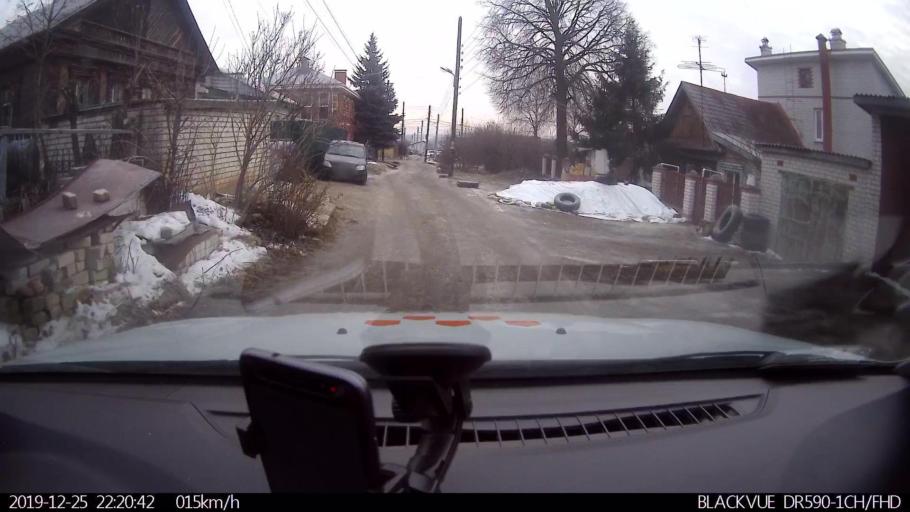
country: RU
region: Nizjnij Novgorod
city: Nizhniy Novgorod
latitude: 56.2545
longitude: 43.9956
